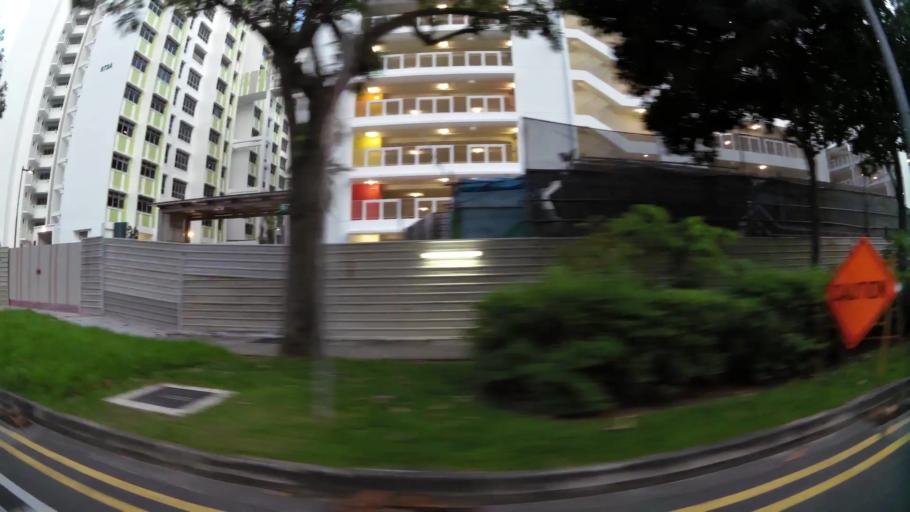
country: MY
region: Johor
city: Kampung Pasir Gudang Baru
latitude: 1.4199
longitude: 103.8413
